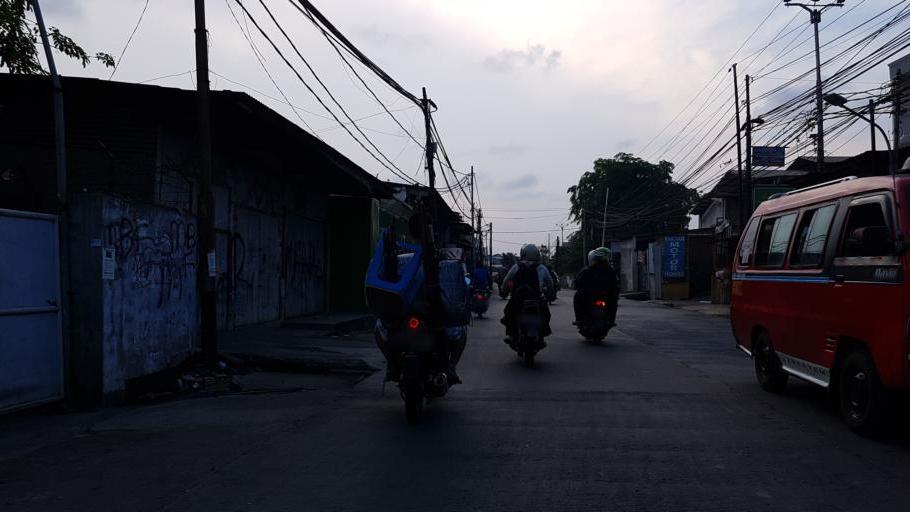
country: ID
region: Jakarta Raya
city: Jakarta
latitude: -6.1412
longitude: 106.7709
